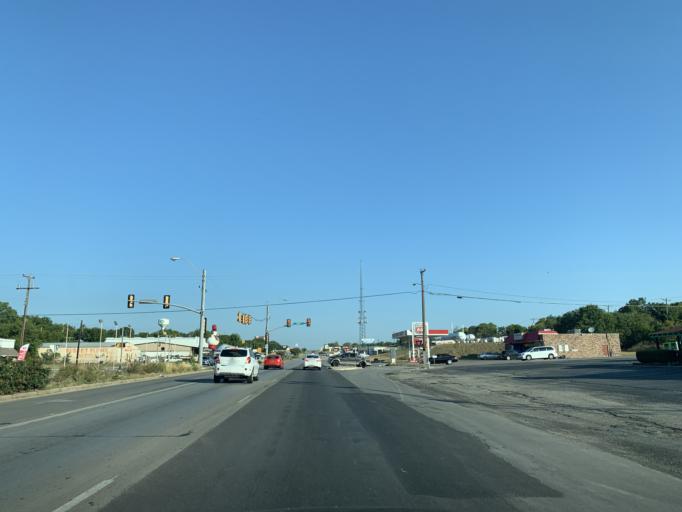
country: US
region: Texas
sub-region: Tarrant County
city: Sansom Park
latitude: 32.7986
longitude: -97.4047
